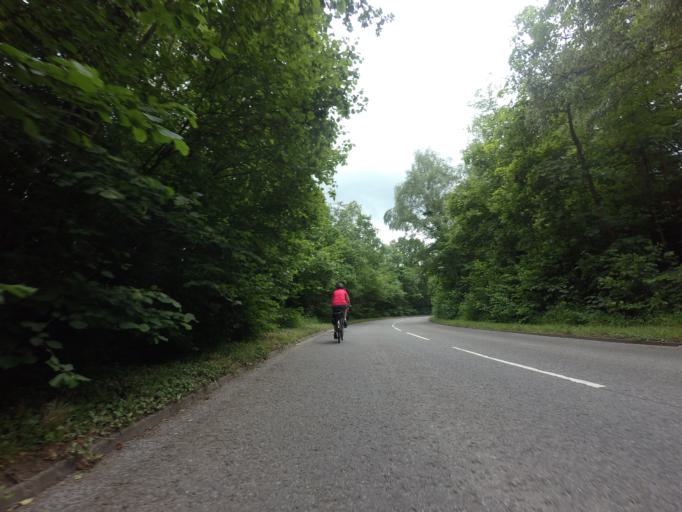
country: GB
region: England
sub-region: Kent
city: Gillingham
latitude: 51.4098
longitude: 0.5263
